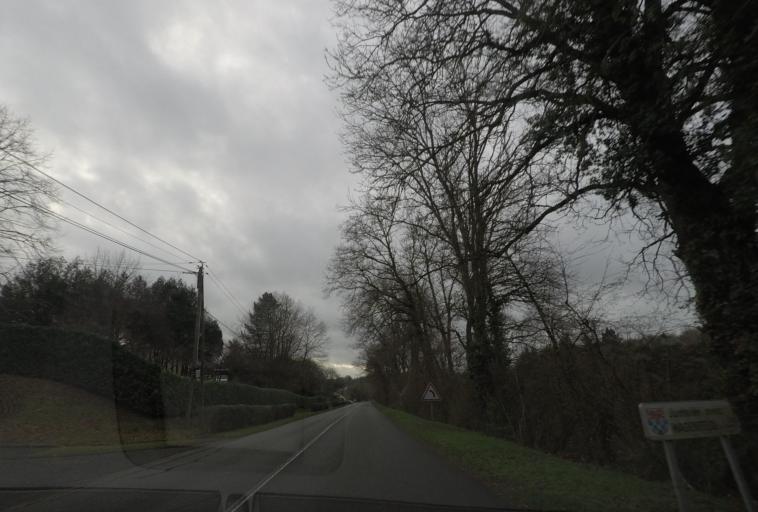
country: FR
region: Pays de la Loire
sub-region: Departement de la Sarthe
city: Vibraye
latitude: 47.9972
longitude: 0.7629
